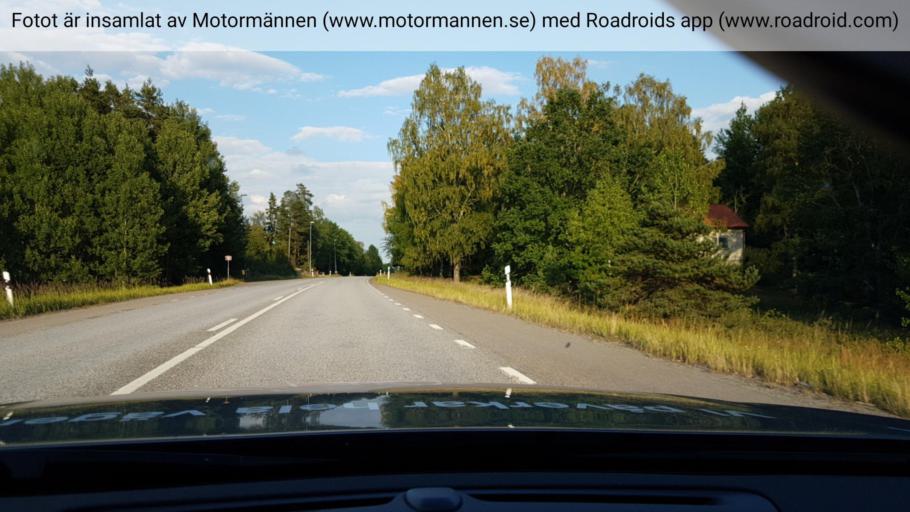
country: SE
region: Uppsala
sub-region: Heby Kommun
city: Morgongava
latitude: 59.8934
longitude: 17.1497
